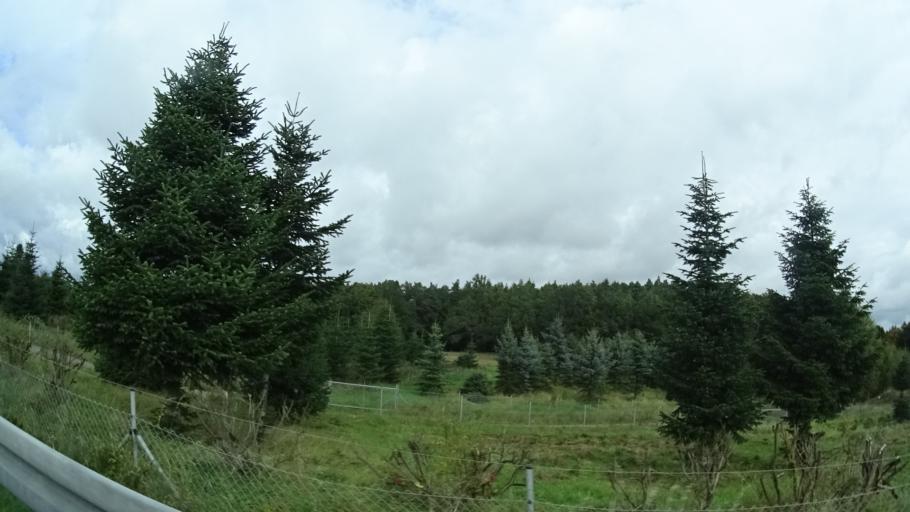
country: DE
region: Bavaria
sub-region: Upper Franconia
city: Priesendorf
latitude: 49.9032
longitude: 10.6824
